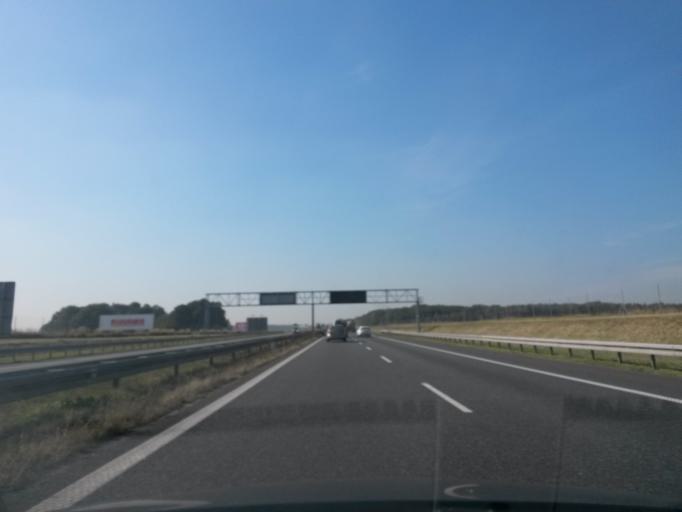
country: PL
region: Silesian Voivodeship
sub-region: Powiat gliwicki
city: Zernica
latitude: 50.2617
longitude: 18.6365
